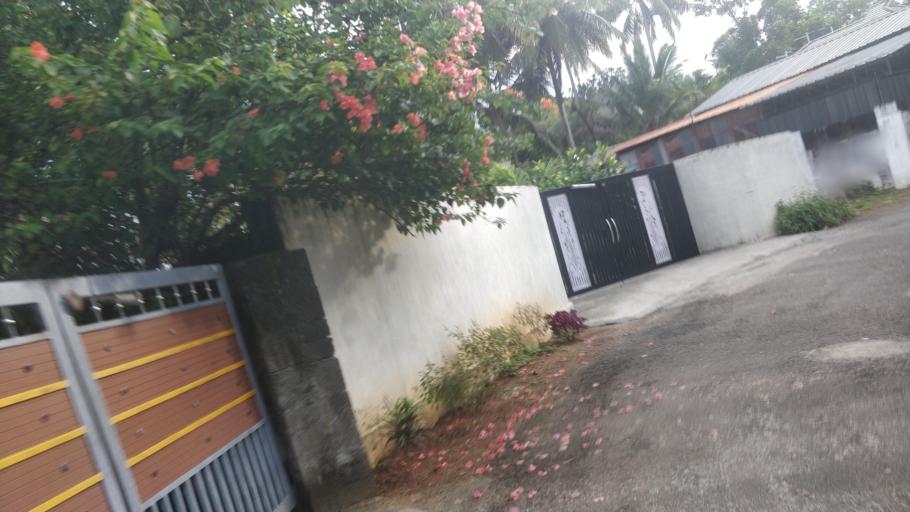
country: IN
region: Kerala
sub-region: Alappuzha
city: Shertallai
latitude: 9.6937
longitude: 76.3628
